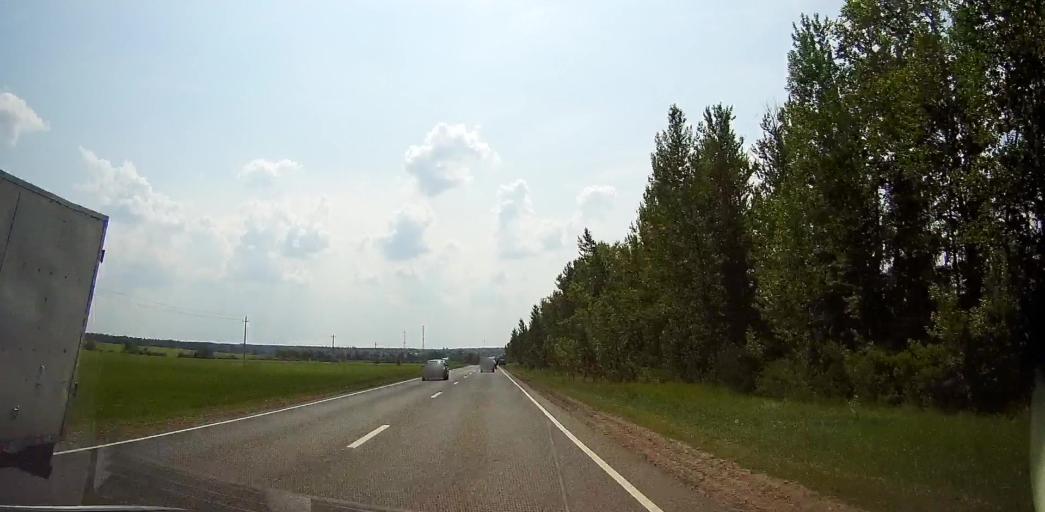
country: RU
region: Moskovskaya
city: Malino
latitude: 55.0757
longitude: 38.1628
